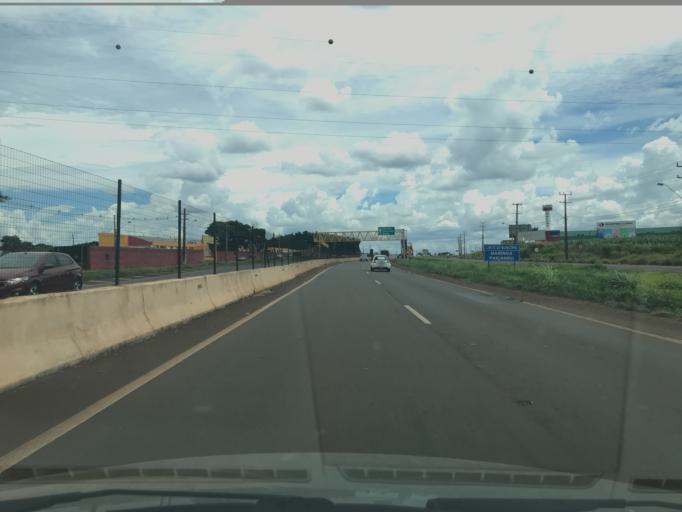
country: BR
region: Parana
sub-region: Paicandu
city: Paicandu
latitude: -23.4530
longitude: -52.0101
